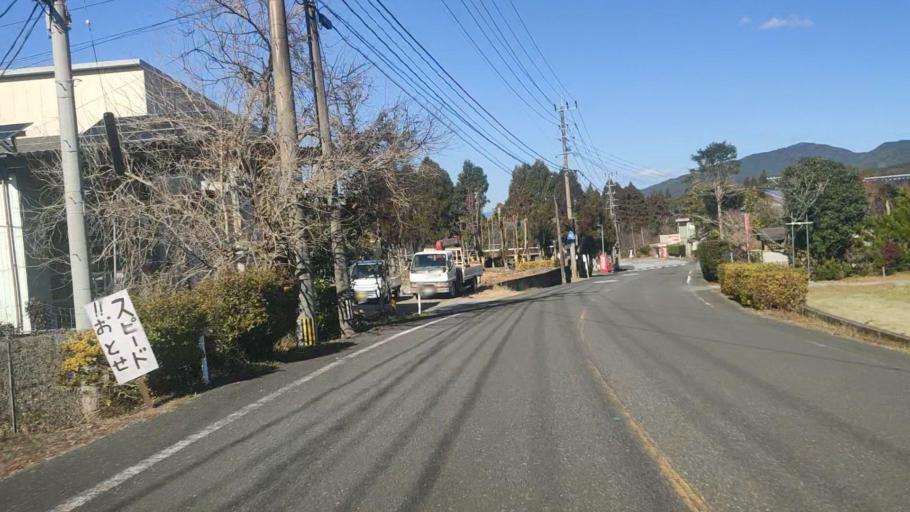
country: JP
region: Oita
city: Saiki
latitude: 32.9025
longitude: 131.9333
